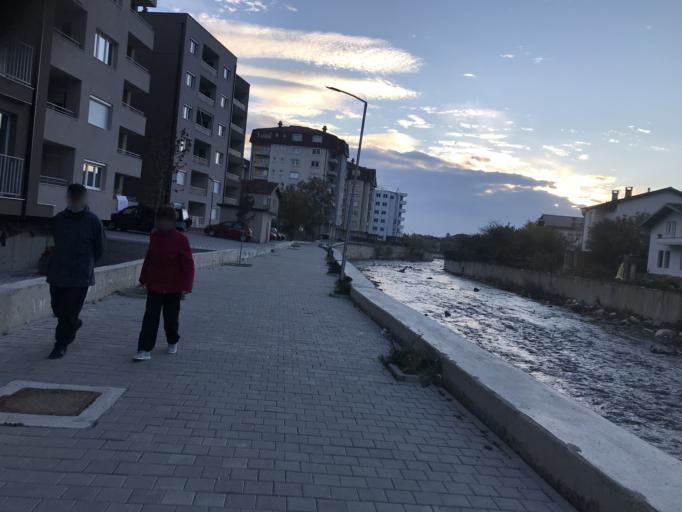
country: XK
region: Pec
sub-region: Komuna e Pejes
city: Peje
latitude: 42.6595
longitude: 20.2746
